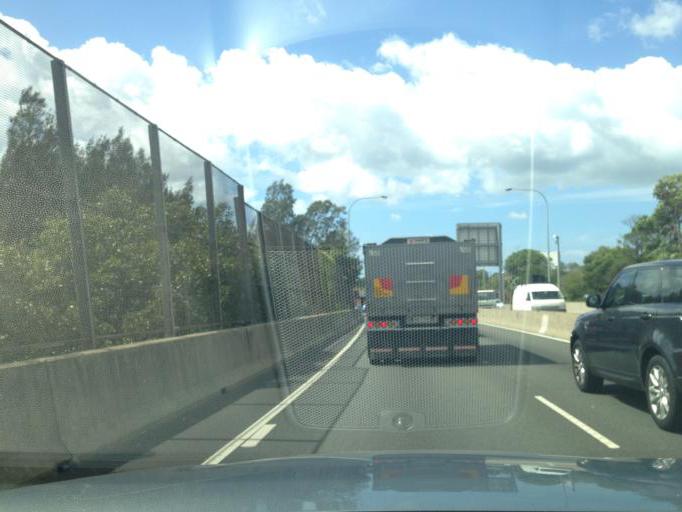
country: AU
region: New South Wales
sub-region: Rockdale
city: Arncliffe
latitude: -33.9409
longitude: 151.1567
